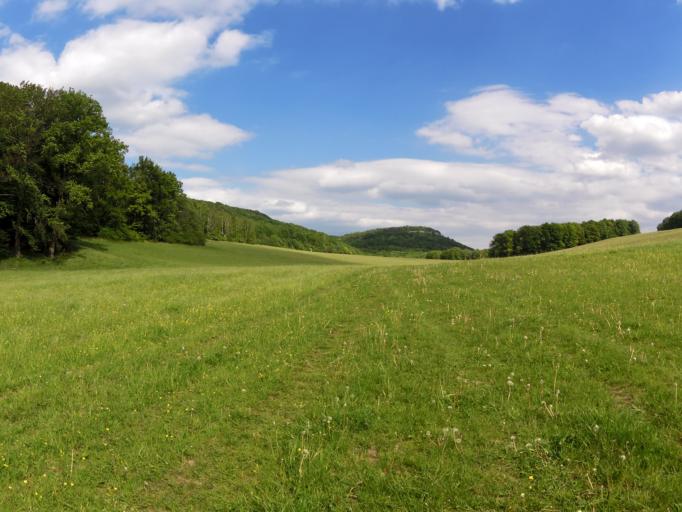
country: DE
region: Thuringia
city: Seebach
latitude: 50.9605
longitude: 10.4345
